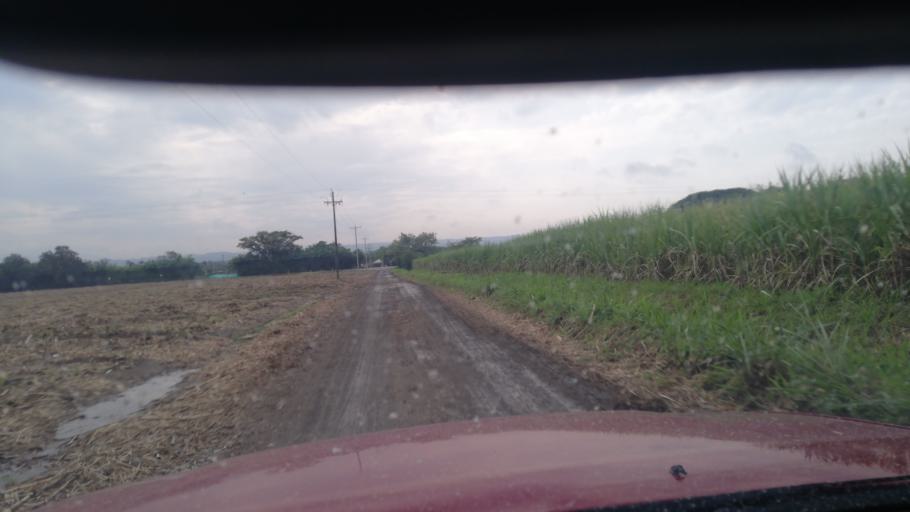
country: CO
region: Risaralda
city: La Virginia
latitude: 4.8736
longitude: -75.9220
